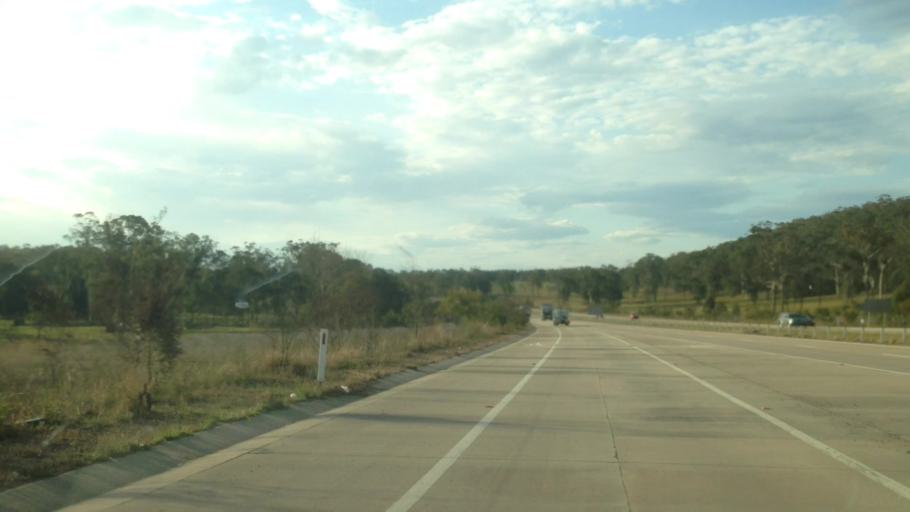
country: AU
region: New South Wales
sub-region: Cessnock
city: Heddon Greta
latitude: -32.8419
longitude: 151.5419
